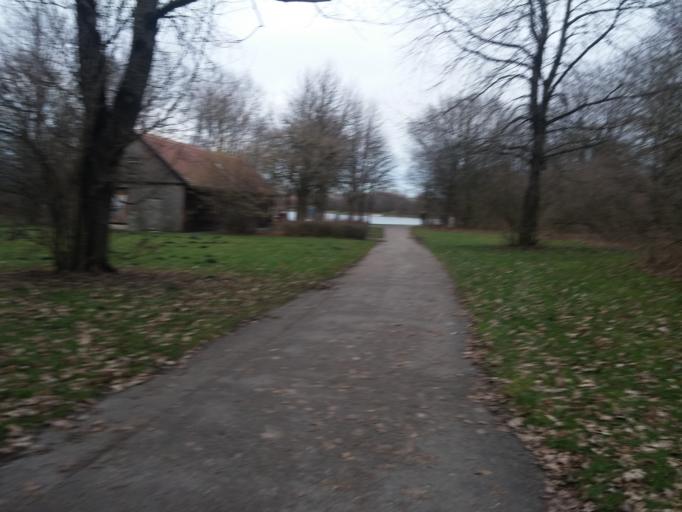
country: DE
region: Bavaria
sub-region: Upper Bavaria
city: Unterfoehring
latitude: 48.1916
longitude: 11.6672
